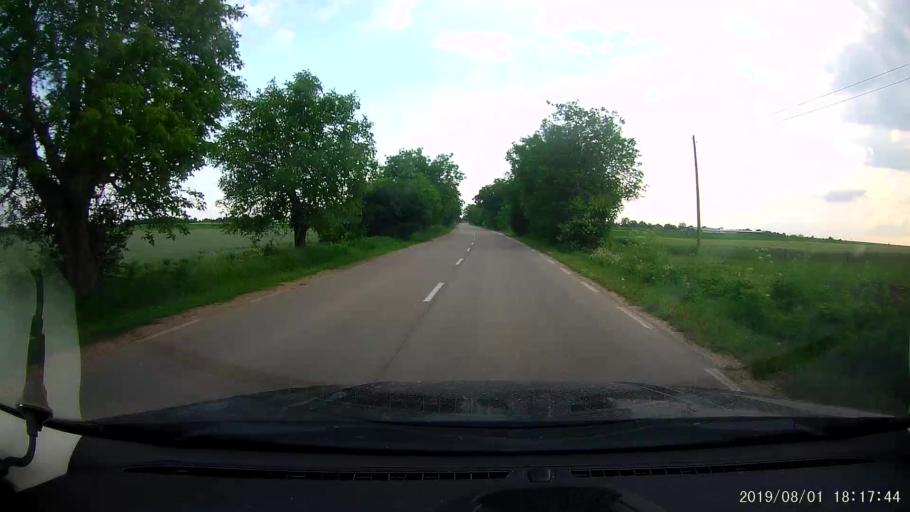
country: BG
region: Shumen
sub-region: Obshtina Kaolinovo
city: Kaolinovo
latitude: 43.7080
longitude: 27.0818
